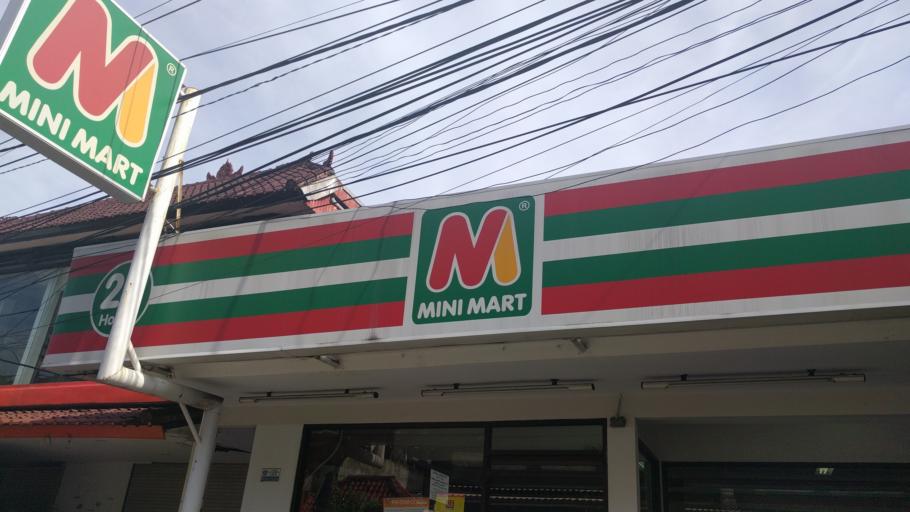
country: ID
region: Bali
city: Kuta
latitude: -8.7100
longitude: 115.1737
